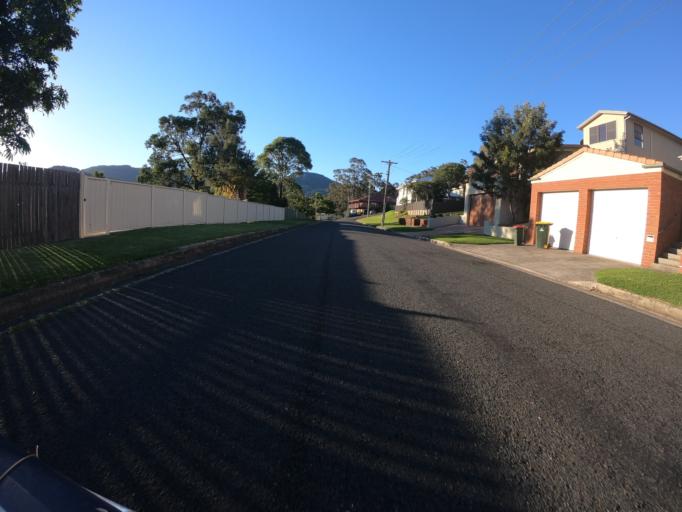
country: AU
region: New South Wales
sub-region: Wollongong
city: West Wollongong
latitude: -34.4329
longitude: 150.8538
